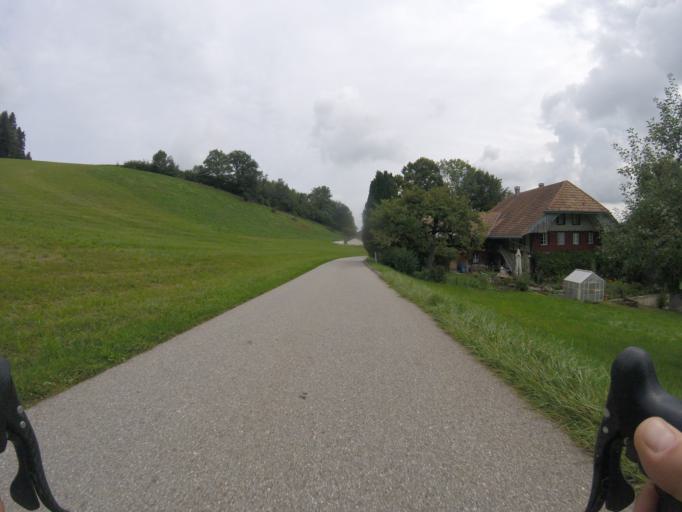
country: CH
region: Bern
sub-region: Emmental District
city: Lutzelfluh
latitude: 46.9730
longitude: 7.6720
